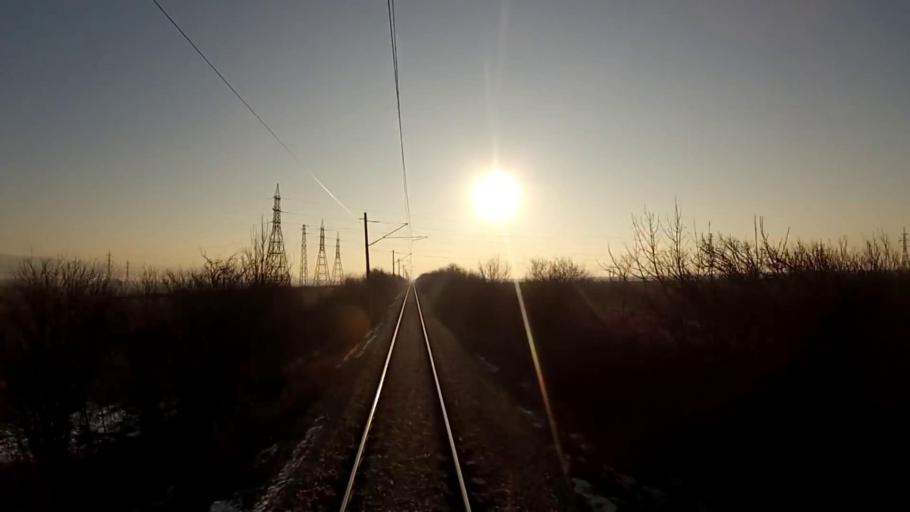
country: BG
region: Sofiya
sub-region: Obshtina Kostinbrod
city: Kostinbrod
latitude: 42.8165
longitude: 23.1796
